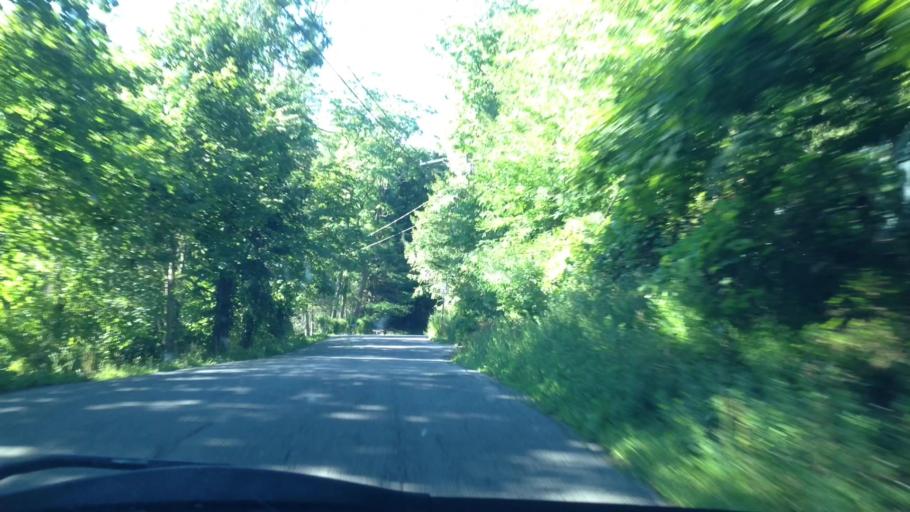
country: US
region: New York
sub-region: Ulster County
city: Tillson
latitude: 41.8117
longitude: -74.0439
